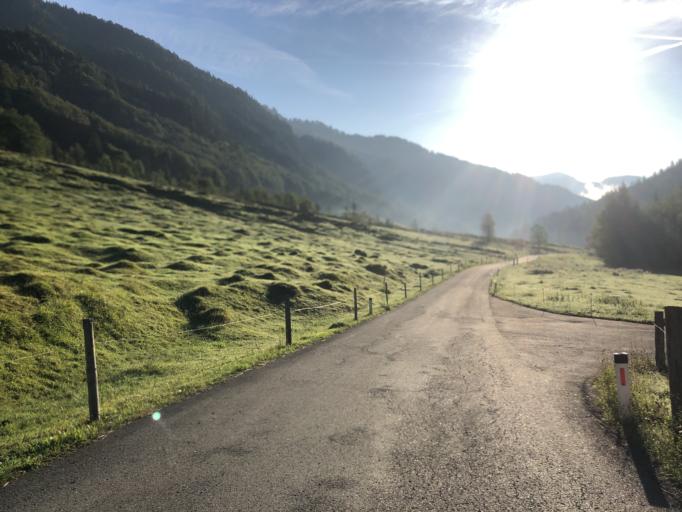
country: AT
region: Tyrol
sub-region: Politischer Bezirk Kitzbuhel
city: Schwendt
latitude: 47.5807
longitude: 12.3383
